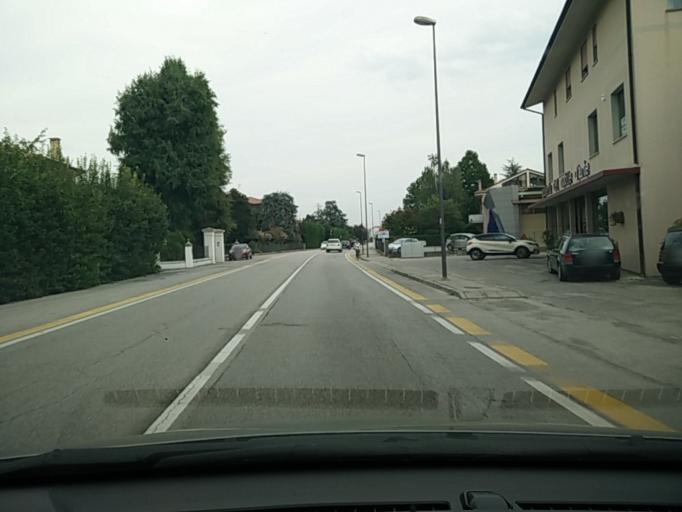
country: IT
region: Veneto
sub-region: Provincia di Treviso
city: Treviso
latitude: 45.6696
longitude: 12.2088
